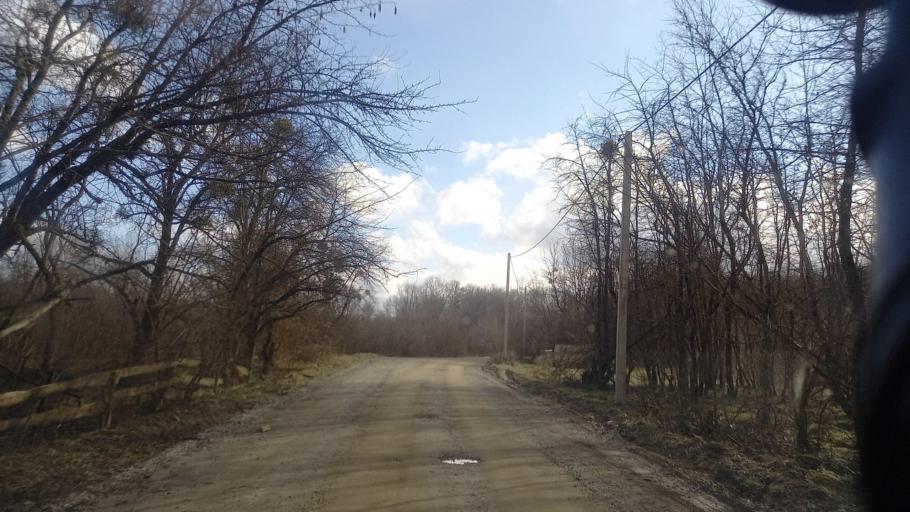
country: RU
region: Krasnodarskiy
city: Smolenskaya
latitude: 44.6035
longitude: 38.8432
